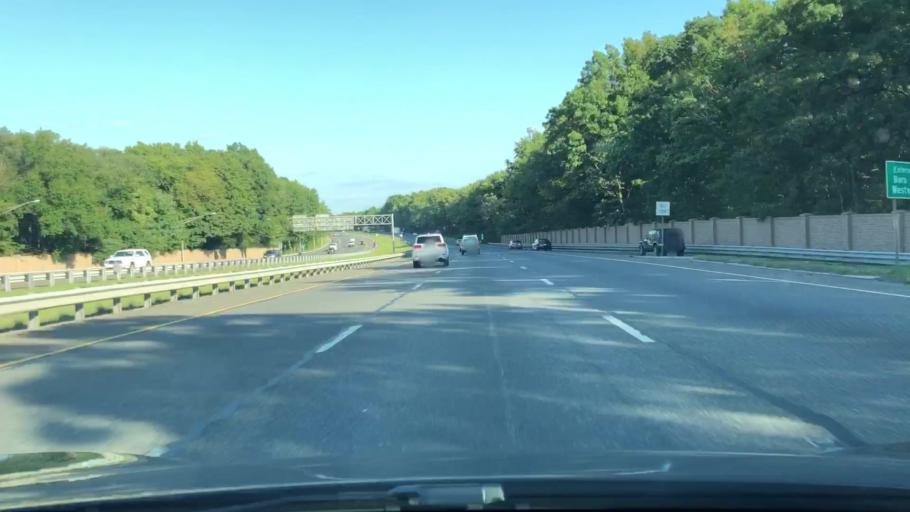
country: US
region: New Jersey
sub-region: Gloucester County
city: Westville
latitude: 39.8593
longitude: -75.1344
